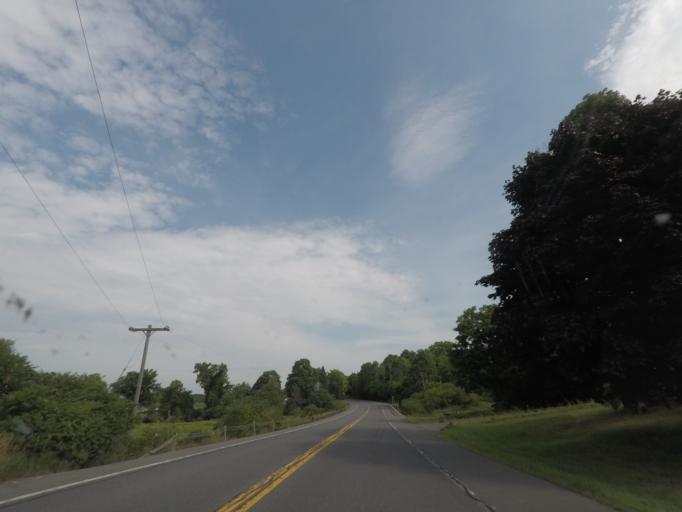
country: US
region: New York
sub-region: Rensselaer County
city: Poestenkill
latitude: 42.7020
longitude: -73.5619
